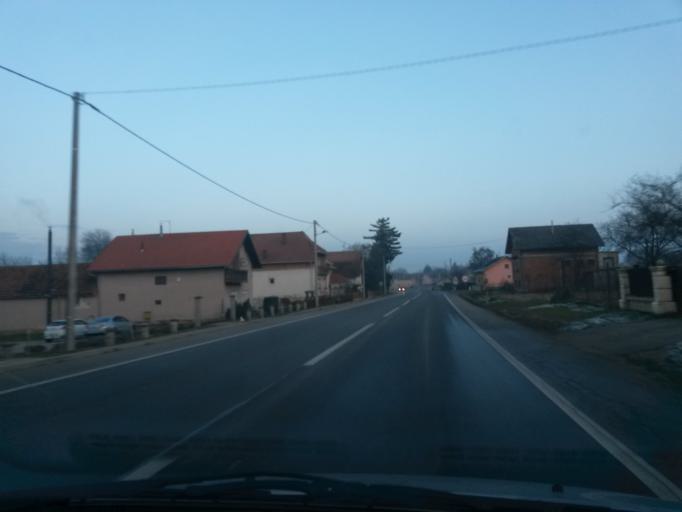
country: HR
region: Varazdinska
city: Ludbreg
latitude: 46.2368
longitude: 16.6425
